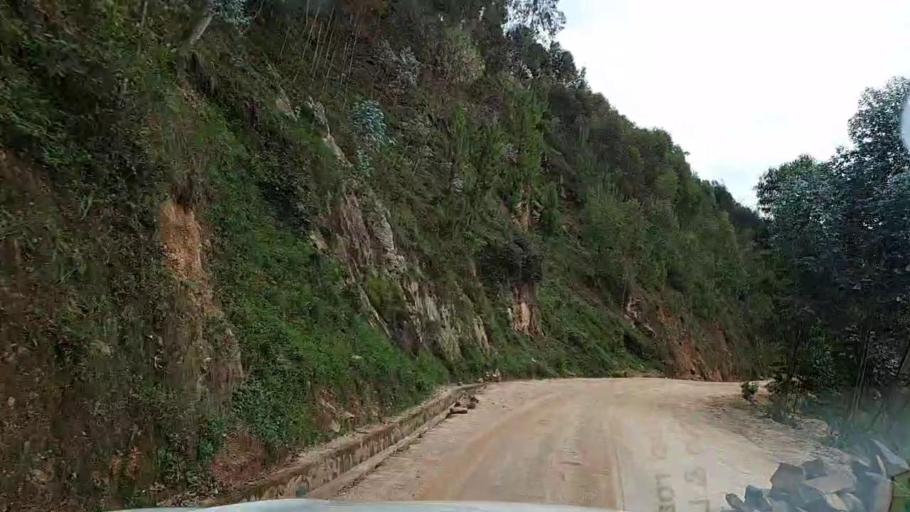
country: RW
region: Southern Province
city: Nzega
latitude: -2.3683
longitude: 29.4508
